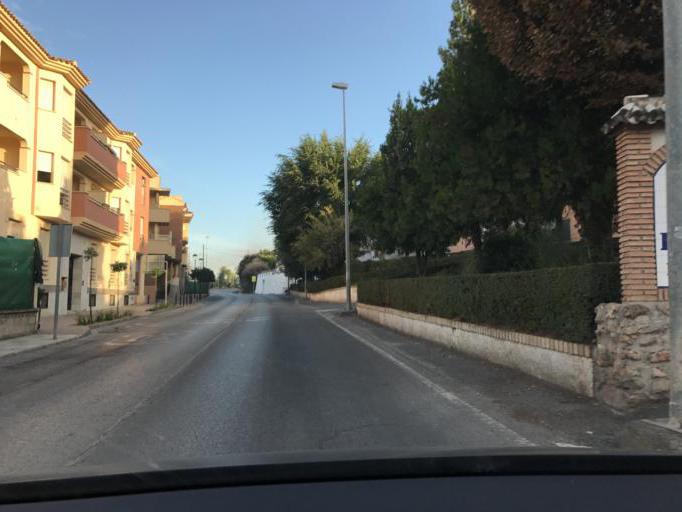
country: ES
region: Andalusia
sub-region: Provincia de Granada
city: Pulianas
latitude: 37.2216
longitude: -3.6097
